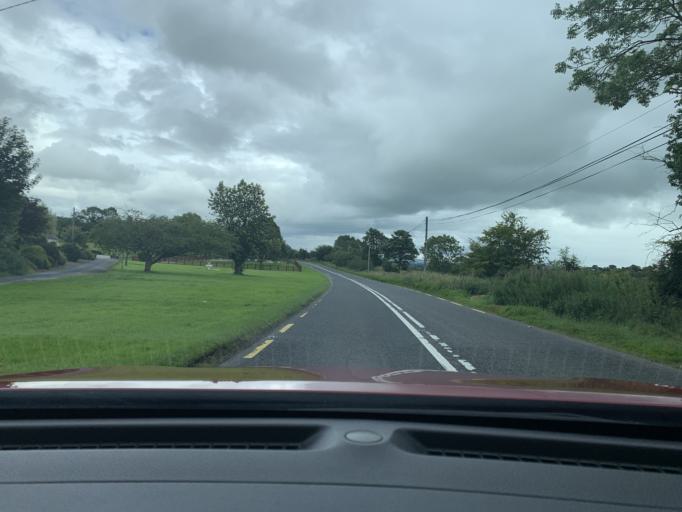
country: IE
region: Ulster
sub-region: County Donegal
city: Convoy
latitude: 54.8008
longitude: -7.6252
